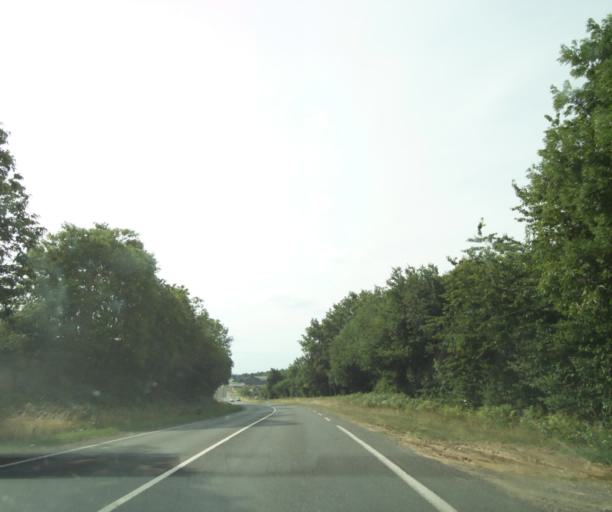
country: FR
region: Pays de la Loire
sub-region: Departement de la Sarthe
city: Ecommoy
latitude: 47.8205
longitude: 0.2973
